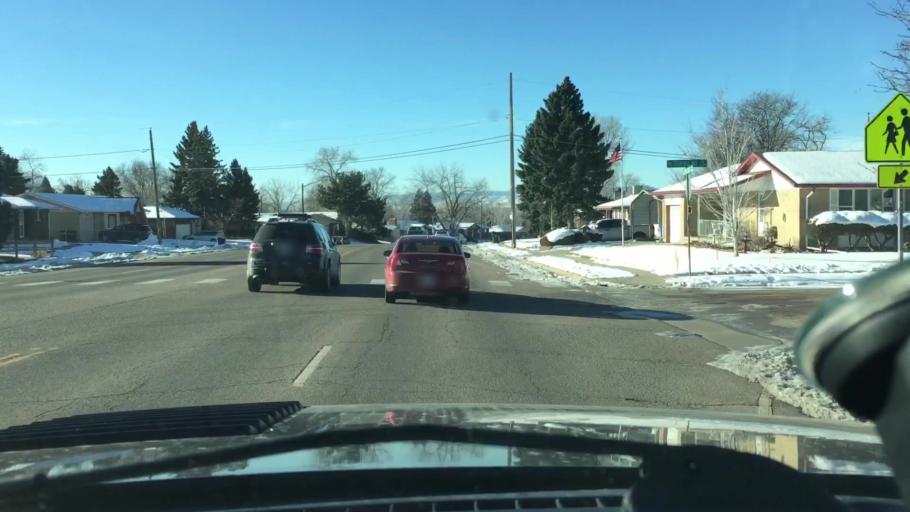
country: US
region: Colorado
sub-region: Adams County
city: Sherrelwood
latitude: 39.8439
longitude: -104.9984
